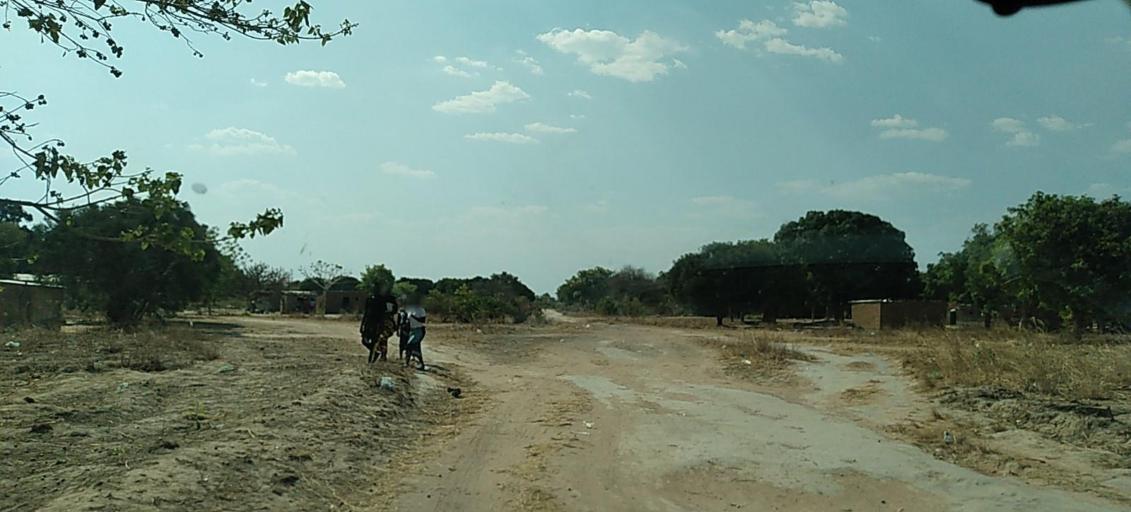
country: ZM
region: North-Western
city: Kalengwa
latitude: -13.1295
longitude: 25.0109
